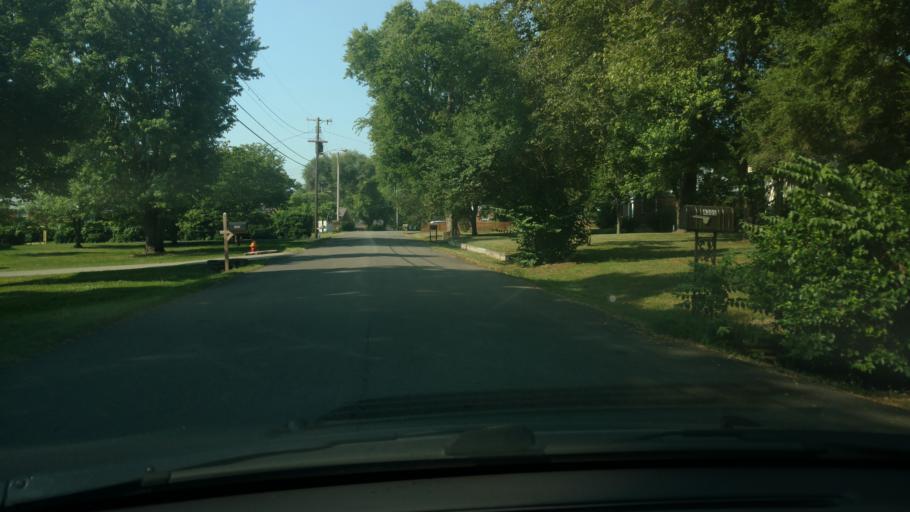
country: US
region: Tennessee
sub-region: Davidson County
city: Lakewood
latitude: 36.2226
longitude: -86.7134
